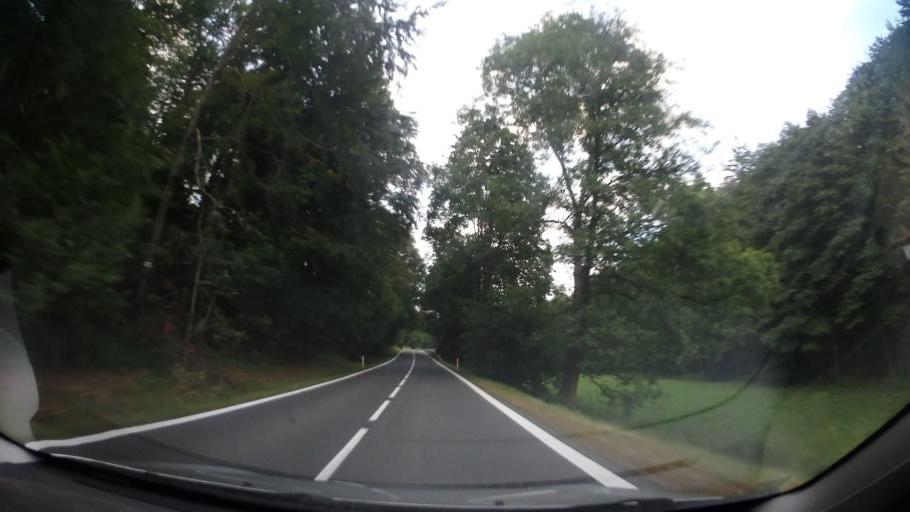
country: CZ
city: Rymarov
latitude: 49.8891
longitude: 17.2547
